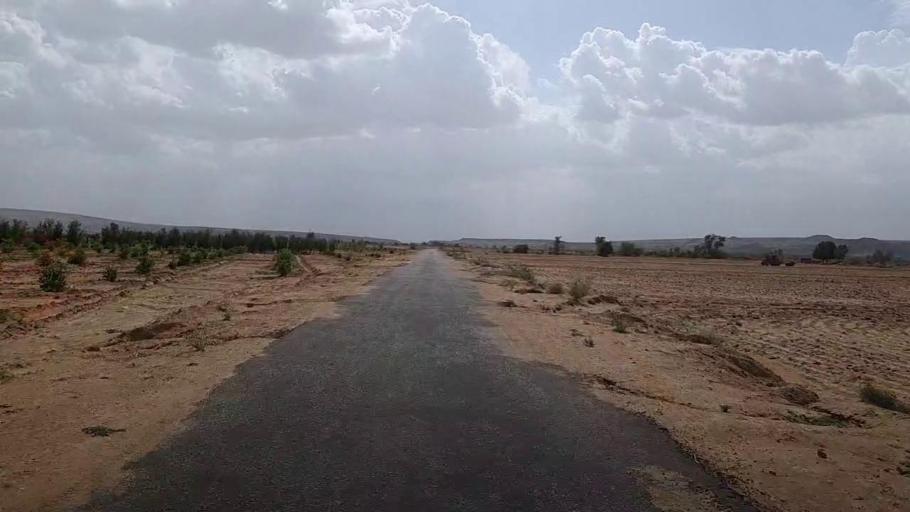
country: PK
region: Sindh
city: Jamshoro
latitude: 25.4031
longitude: 67.7760
